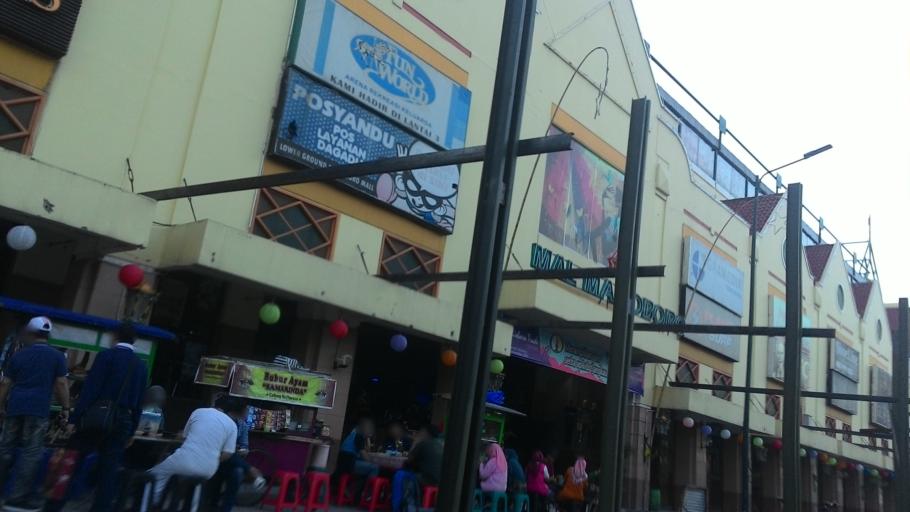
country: ID
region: Daerah Istimewa Yogyakarta
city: Yogyakarta
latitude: -7.7928
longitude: 110.3658
